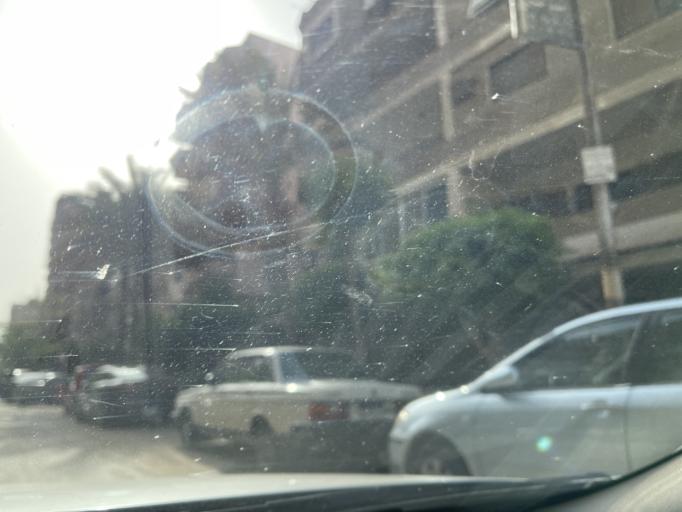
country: EG
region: Muhafazat al Qahirah
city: Cairo
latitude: 30.0662
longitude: 31.3558
